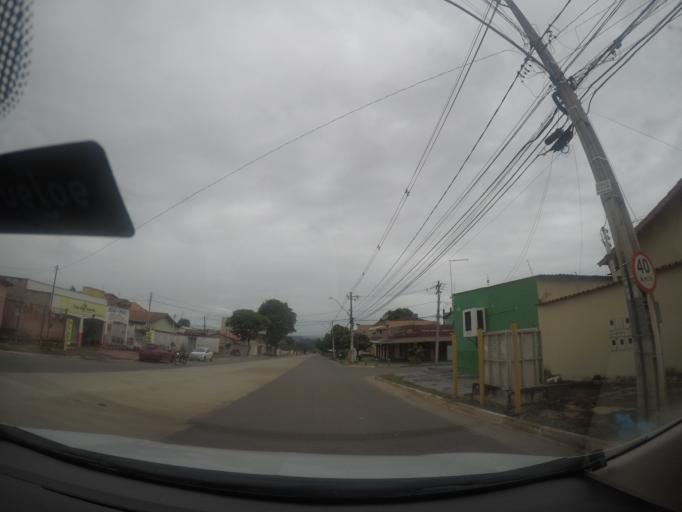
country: BR
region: Goias
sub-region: Goiania
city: Goiania
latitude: -16.6194
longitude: -49.3019
